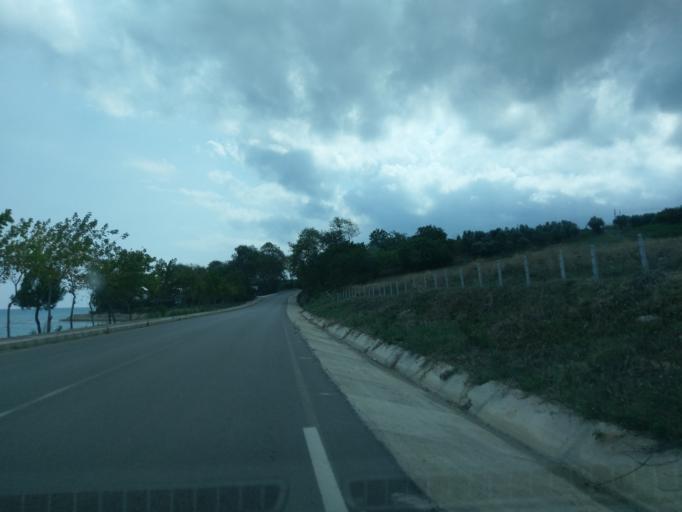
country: TR
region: Sinop
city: Gerze
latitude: 41.8229
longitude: 35.1694
